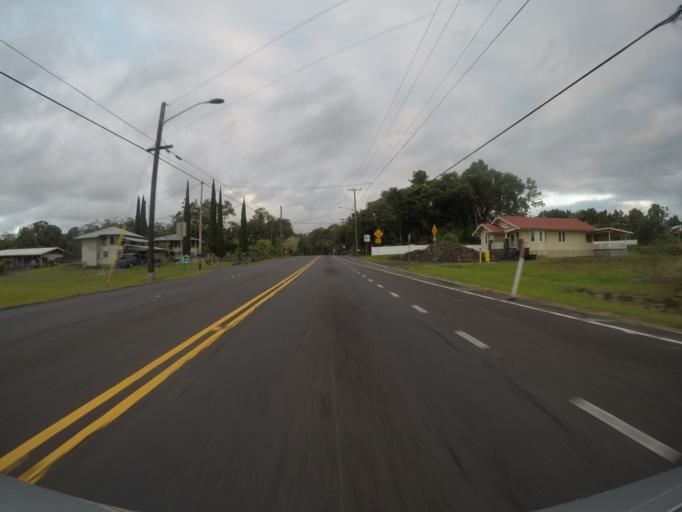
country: US
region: Hawaii
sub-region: Hawaii County
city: Hilo
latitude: 19.6757
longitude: -155.0668
